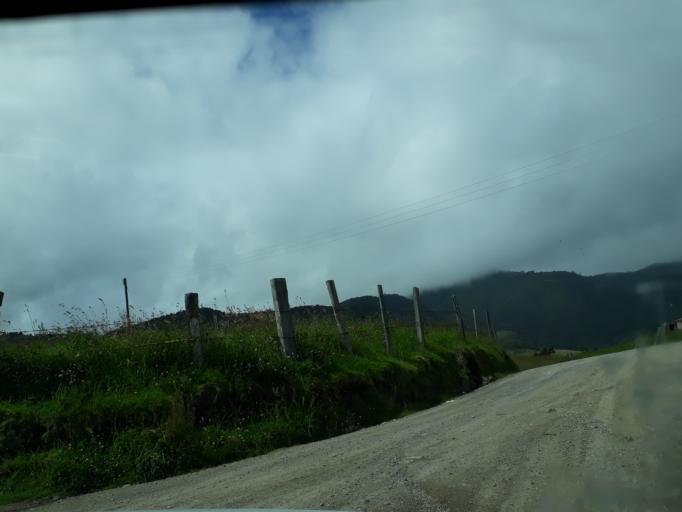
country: CO
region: Cundinamarca
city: La Mesa
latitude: 5.2755
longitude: -73.9053
